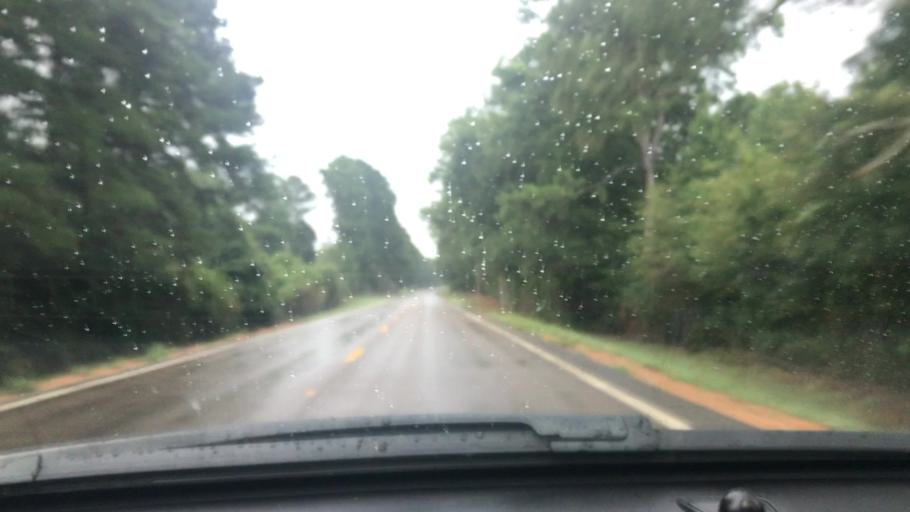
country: US
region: Mississippi
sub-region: Pike County
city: Summit
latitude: 31.3389
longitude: -90.5735
